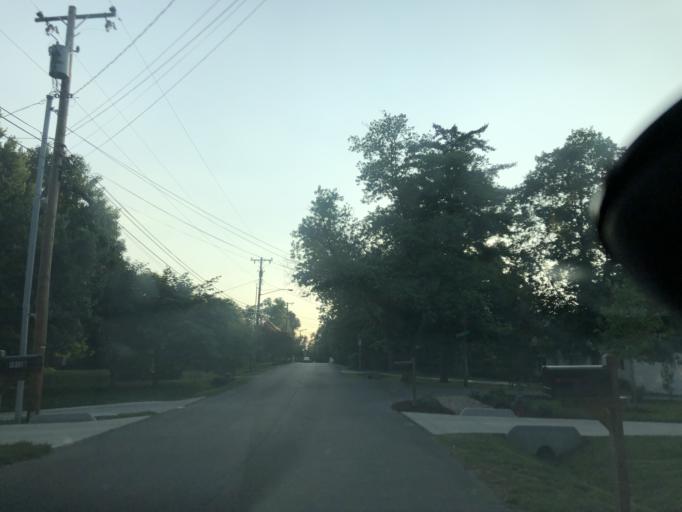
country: US
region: Tennessee
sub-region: Davidson County
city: Oak Hill
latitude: 36.1074
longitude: -86.7907
